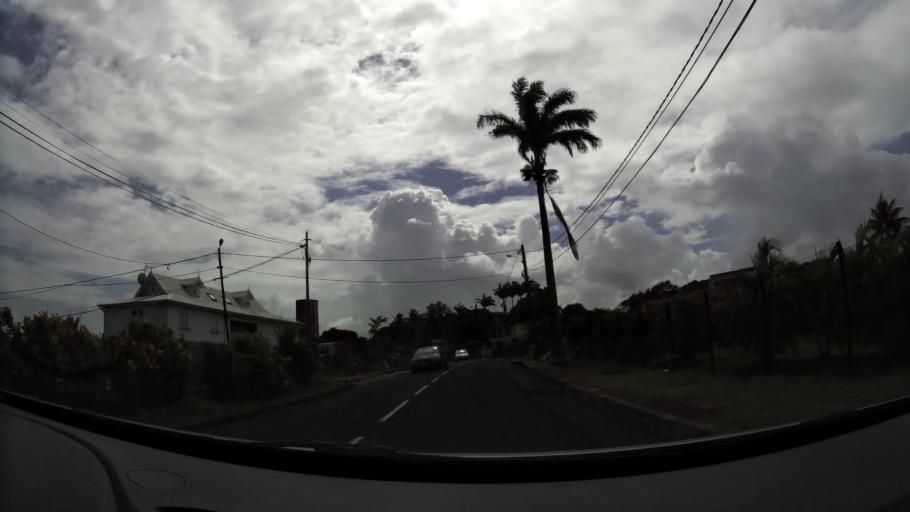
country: MQ
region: Martinique
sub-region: Martinique
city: Saint-Joseph
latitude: 14.6407
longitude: -61.0422
